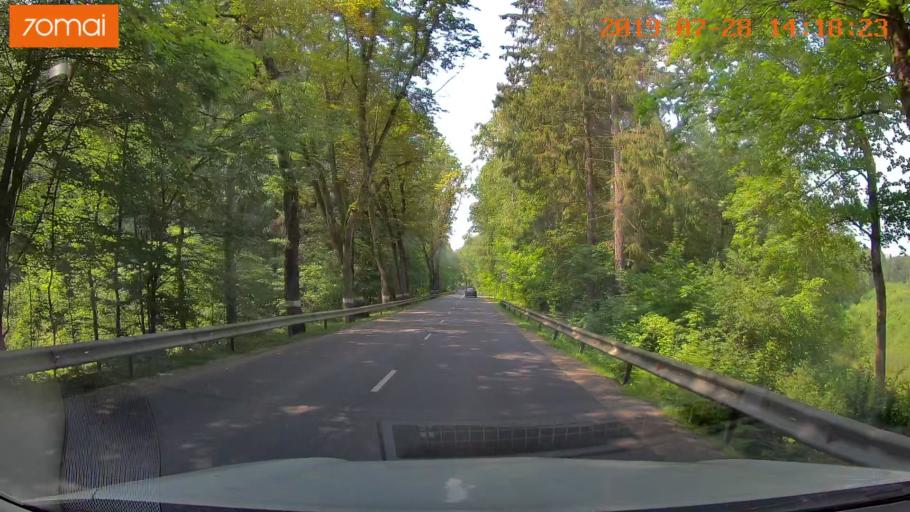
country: RU
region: Kaliningrad
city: Volochayevskoye
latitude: 54.8170
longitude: 20.2414
